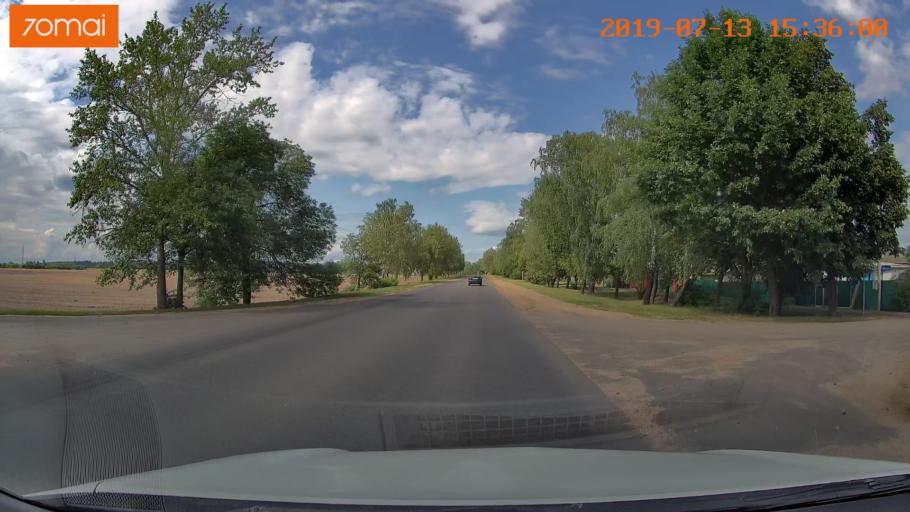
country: BY
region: Mogilev
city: Babruysk
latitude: 53.1275
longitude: 29.1667
